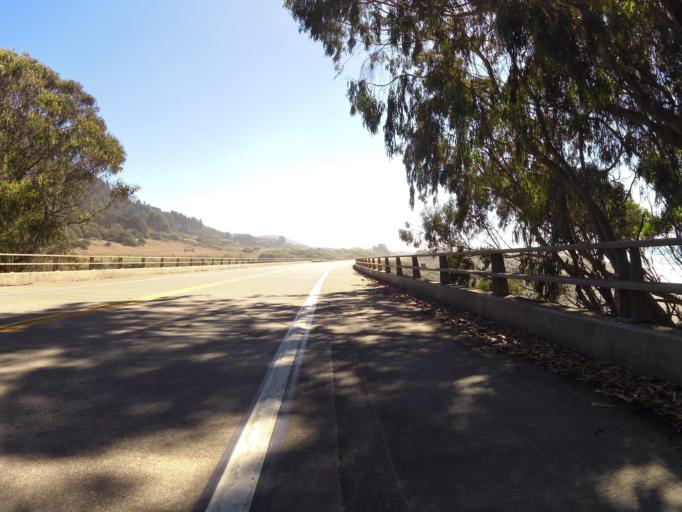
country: US
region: California
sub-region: Mendocino County
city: Fort Bragg
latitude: 39.6784
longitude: -123.7900
